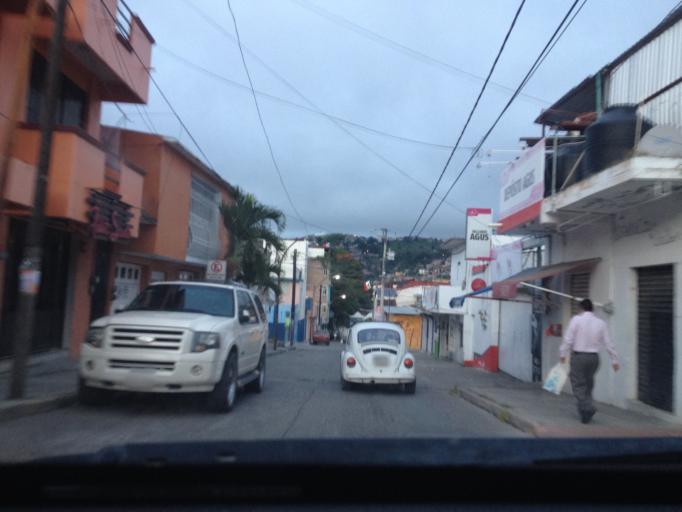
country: MX
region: Guerrero
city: Chilpancingo de los Bravos
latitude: 17.5590
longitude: -99.5036
